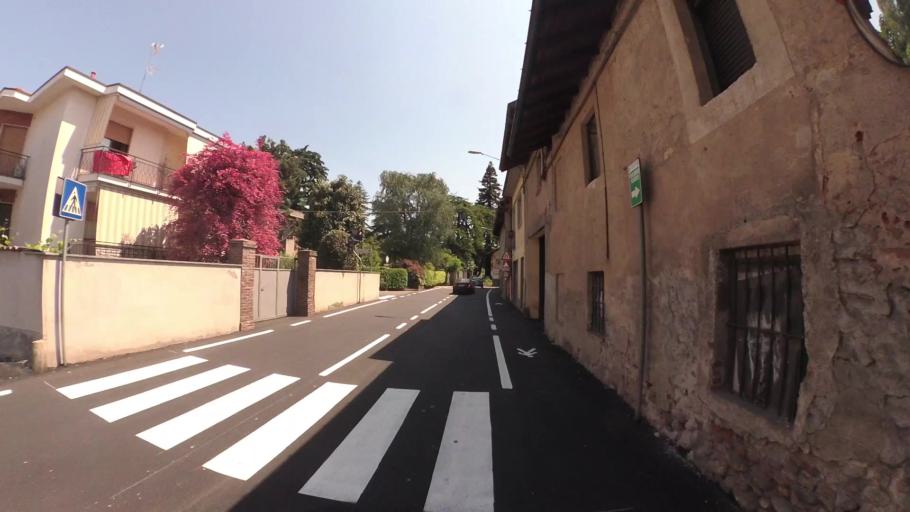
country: IT
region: Lombardy
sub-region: Provincia di Varese
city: Tradate
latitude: 45.7151
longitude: 8.9081
